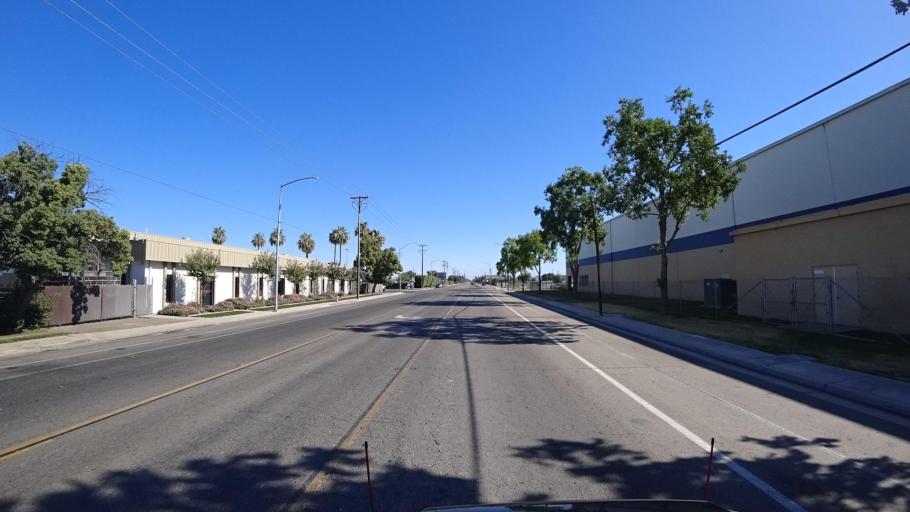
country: US
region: California
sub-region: Fresno County
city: Easton
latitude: 36.6934
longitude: -119.7817
